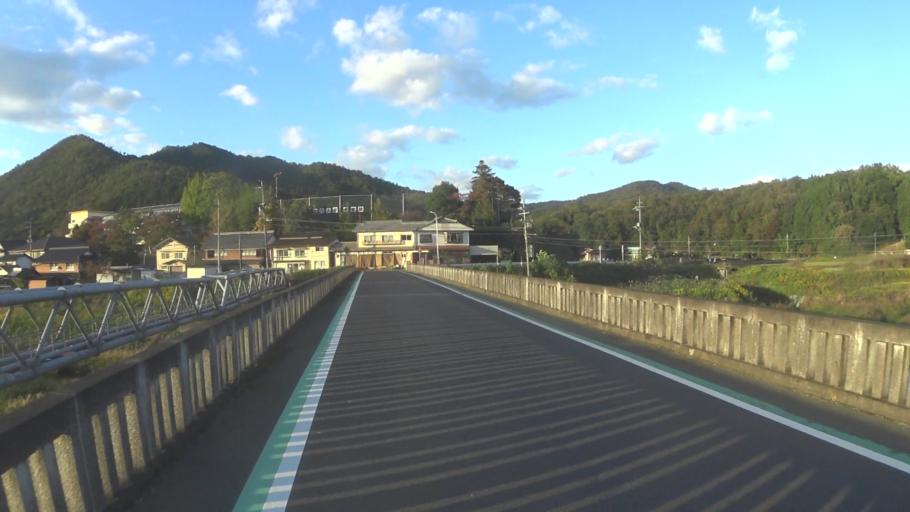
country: JP
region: Kyoto
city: Ayabe
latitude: 35.2512
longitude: 135.2105
